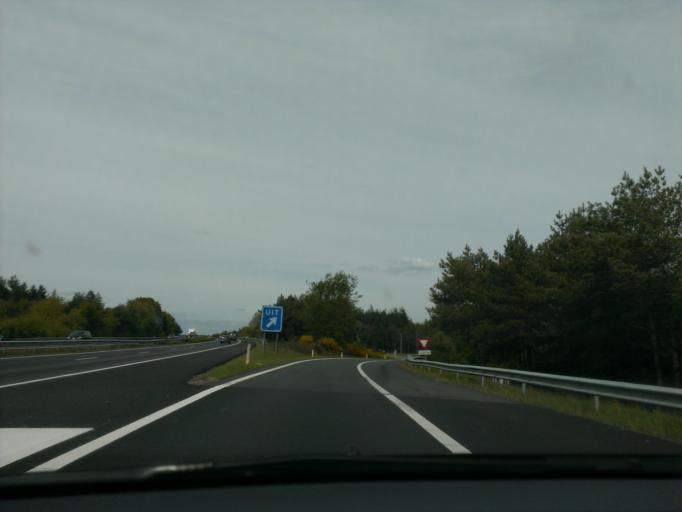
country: NL
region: Gelderland
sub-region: Gemeente Nunspeet
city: Nunspeet
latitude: 52.3729
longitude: 5.8201
